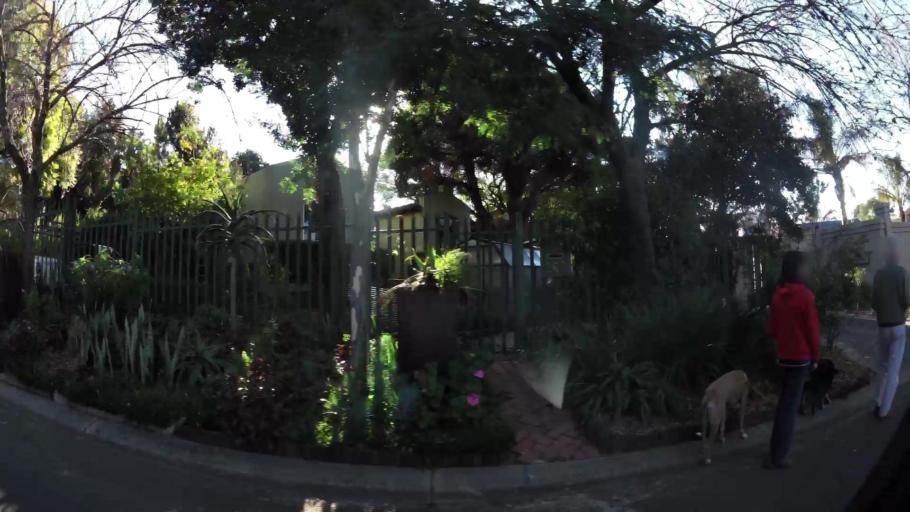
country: ZA
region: Gauteng
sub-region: City of Johannesburg Metropolitan Municipality
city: Roodepoort
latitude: -26.0927
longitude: 27.9554
